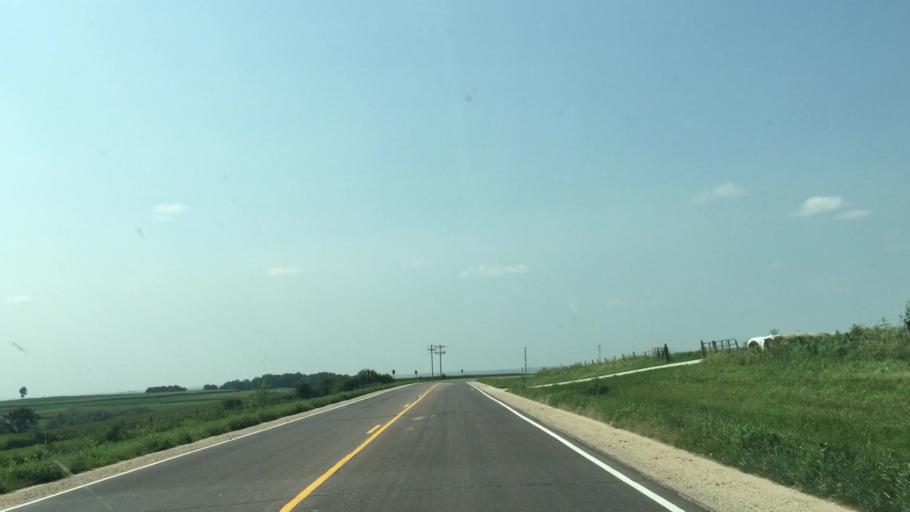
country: US
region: Minnesota
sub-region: Fillmore County
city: Harmony
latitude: 43.6499
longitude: -91.9282
